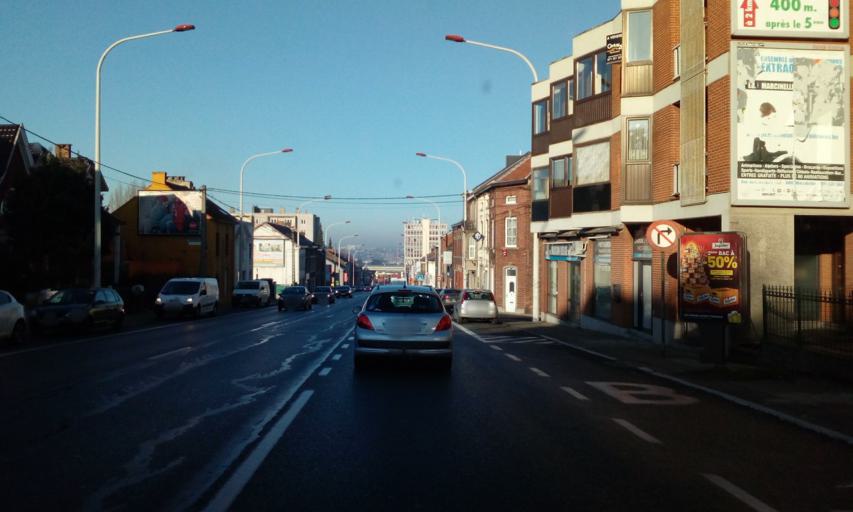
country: BE
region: Wallonia
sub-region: Province du Hainaut
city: Charleroi
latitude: 50.3784
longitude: 4.4662
